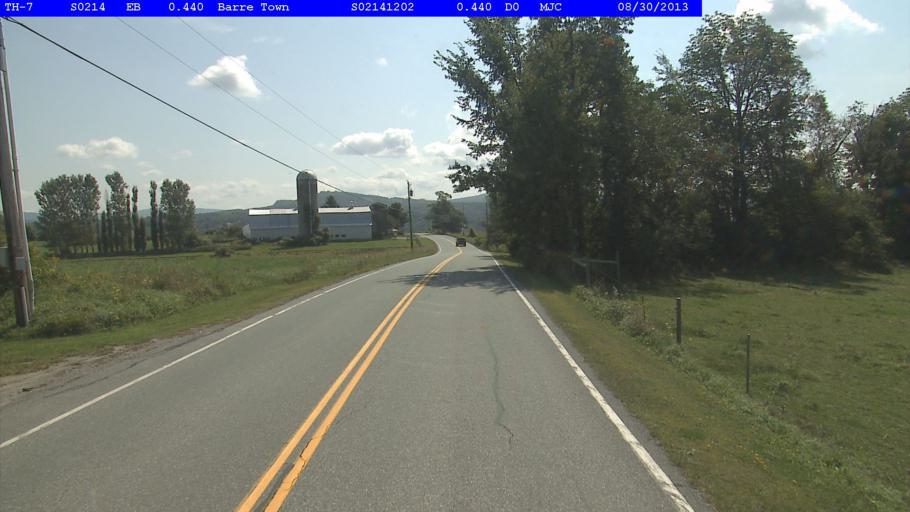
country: US
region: Vermont
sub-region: Washington County
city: South Barre
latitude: 44.1846
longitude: -72.5190
